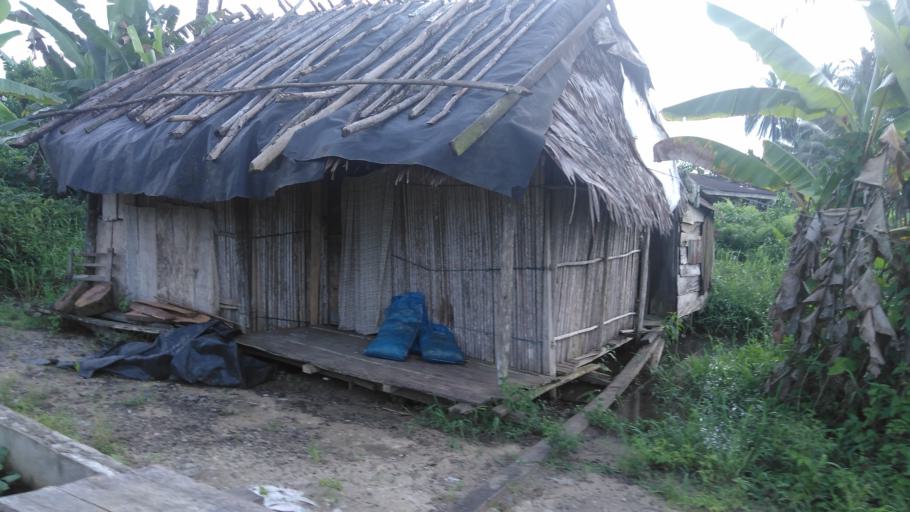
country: NG
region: Edo
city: Siluko
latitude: 6.1447
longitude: 5.1995
